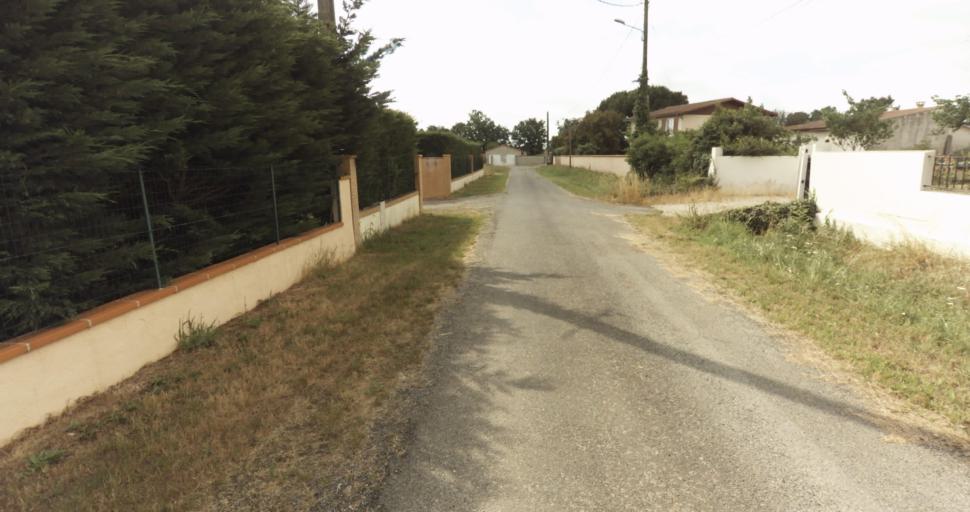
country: FR
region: Midi-Pyrenees
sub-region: Departement de la Haute-Garonne
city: Fonsorbes
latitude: 43.5577
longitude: 1.2233
